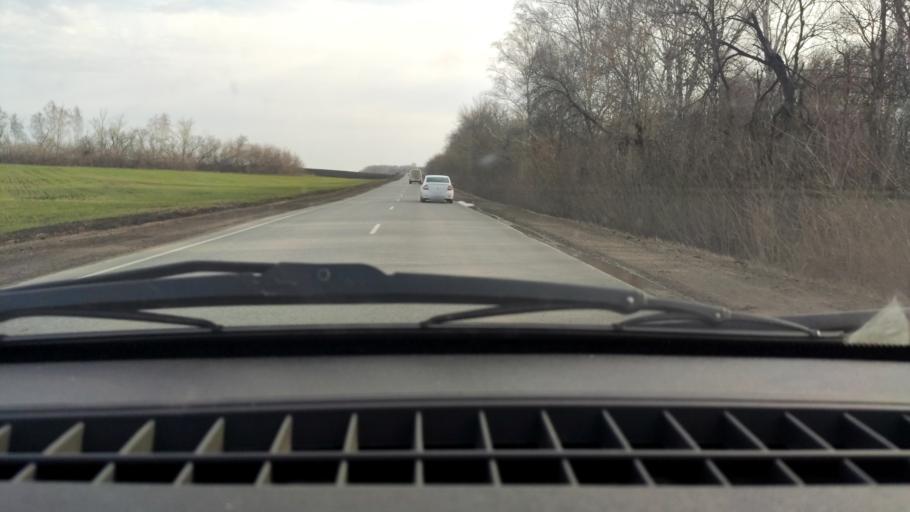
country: RU
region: Bashkortostan
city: Chishmy
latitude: 54.4969
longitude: 55.2812
